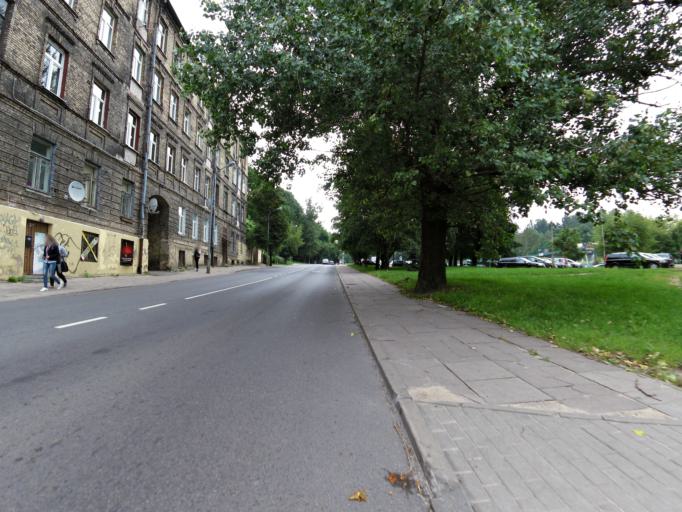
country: LT
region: Vilnius County
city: Rasos
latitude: 54.6703
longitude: 25.2935
